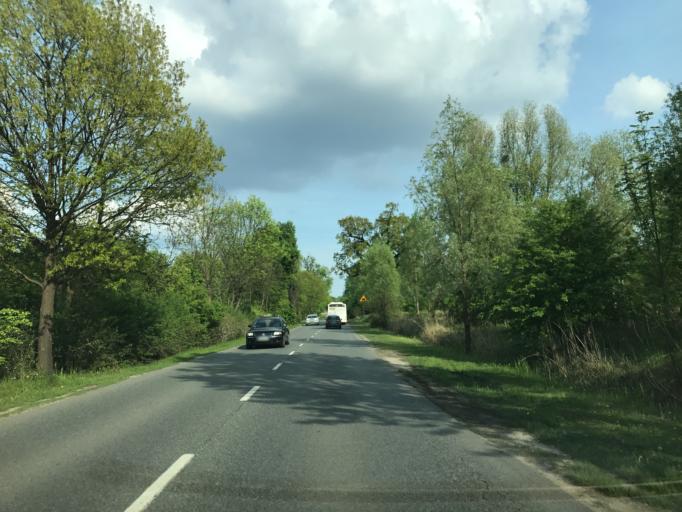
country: PL
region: Kujawsko-Pomorskie
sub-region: Powiat bydgoski
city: Osielsko
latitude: 53.1180
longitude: 18.0892
